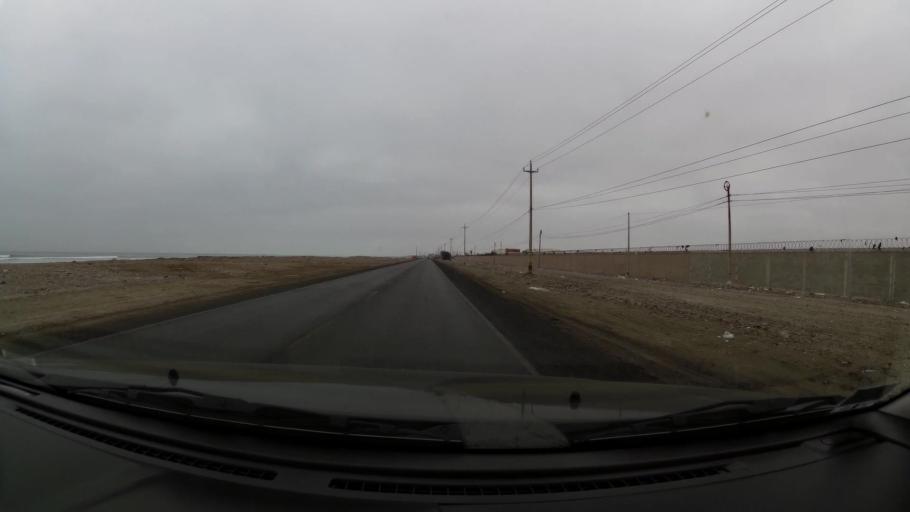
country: PE
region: Ica
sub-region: Provincia de Pisco
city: Pisco
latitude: -13.7515
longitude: -76.2298
